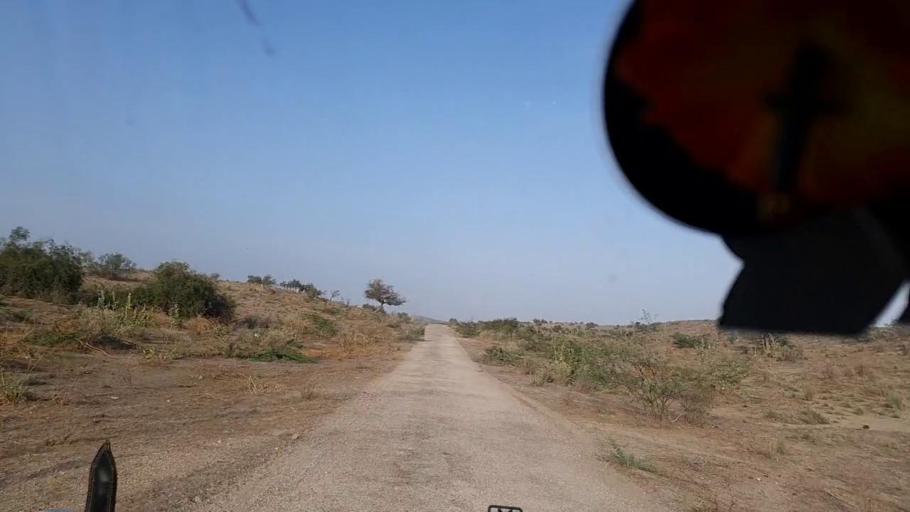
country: PK
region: Sindh
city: Diplo
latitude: 24.5617
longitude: 69.4816
